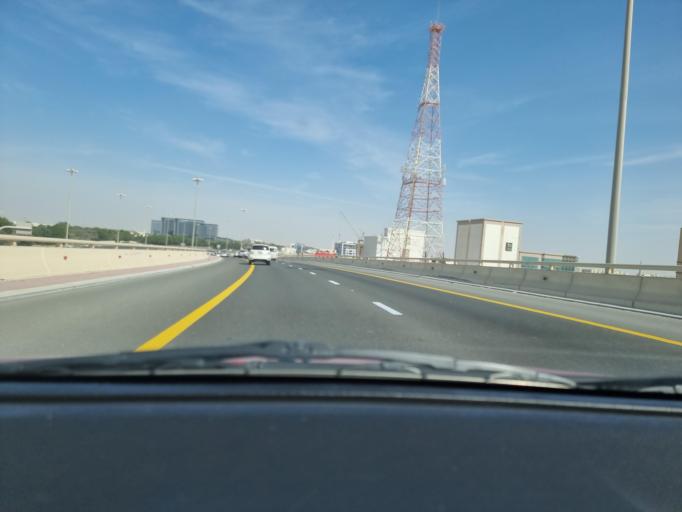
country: AE
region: Abu Dhabi
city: Abu Dhabi
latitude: 24.3117
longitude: 54.6035
